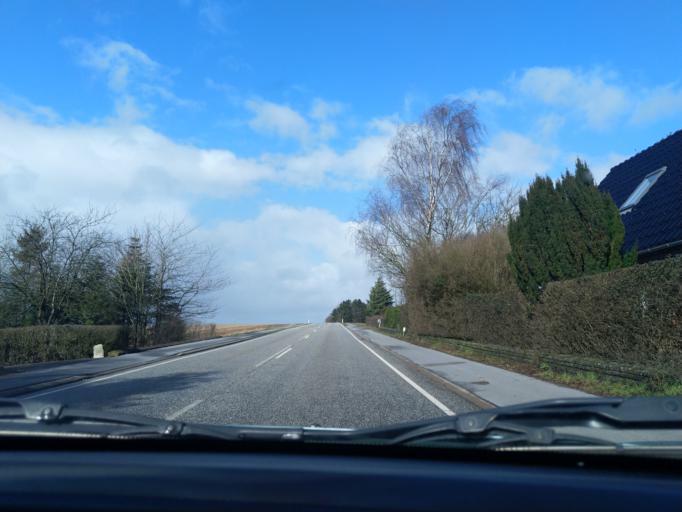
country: DK
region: Zealand
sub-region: Naestved Kommune
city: Naestved
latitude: 55.3076
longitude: 11.6874
